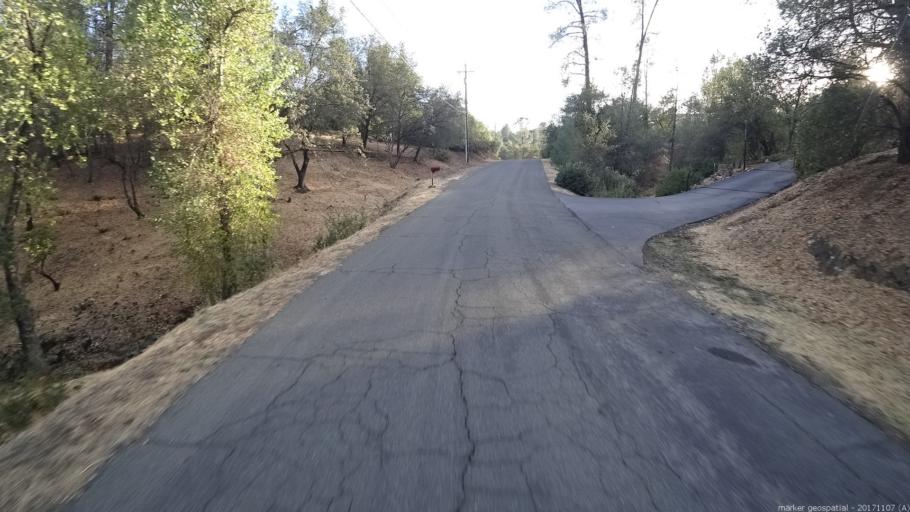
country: US
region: California
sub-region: Shasta County
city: Shasta
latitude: 40.5364
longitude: -122.4835
